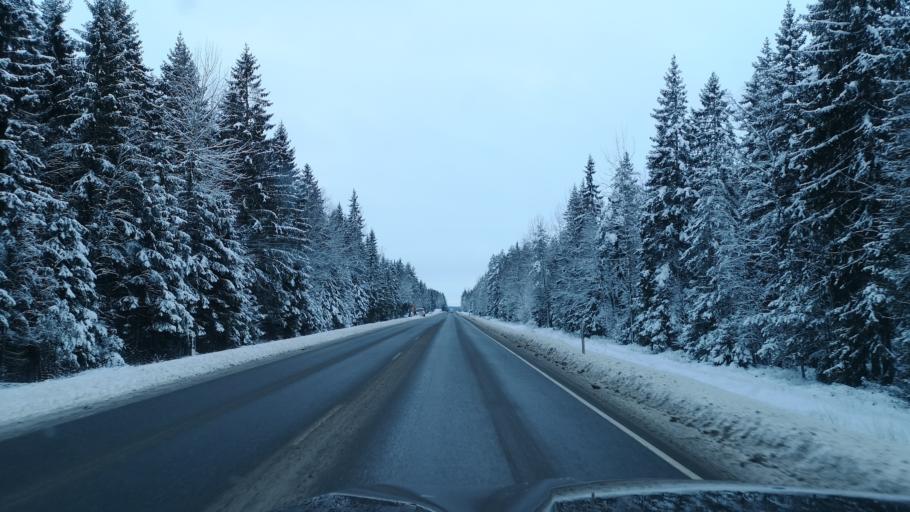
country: FI
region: Varsinais-Suomi
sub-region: Loimaa
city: Loimaa
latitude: 60.9032
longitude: 23.1456
